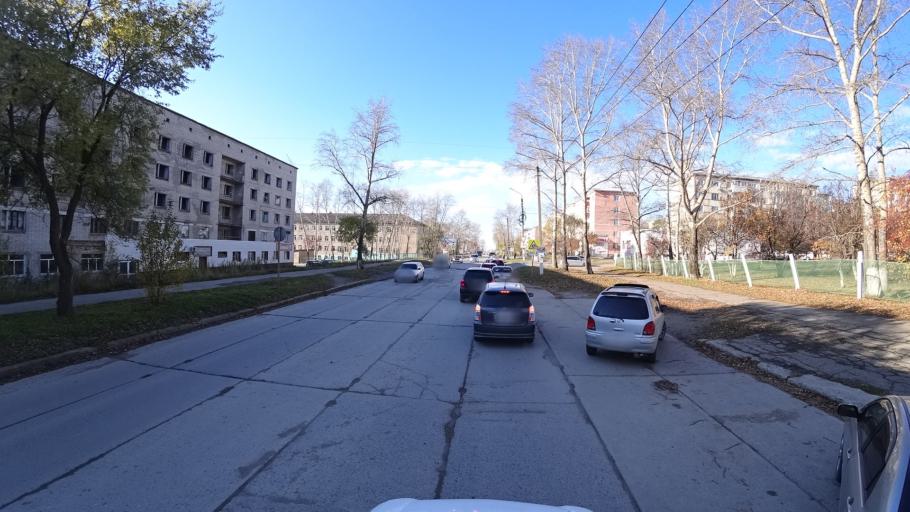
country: RU
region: Khabarovsk Krai
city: Amursk
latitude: 50.2332
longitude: 136.9087
